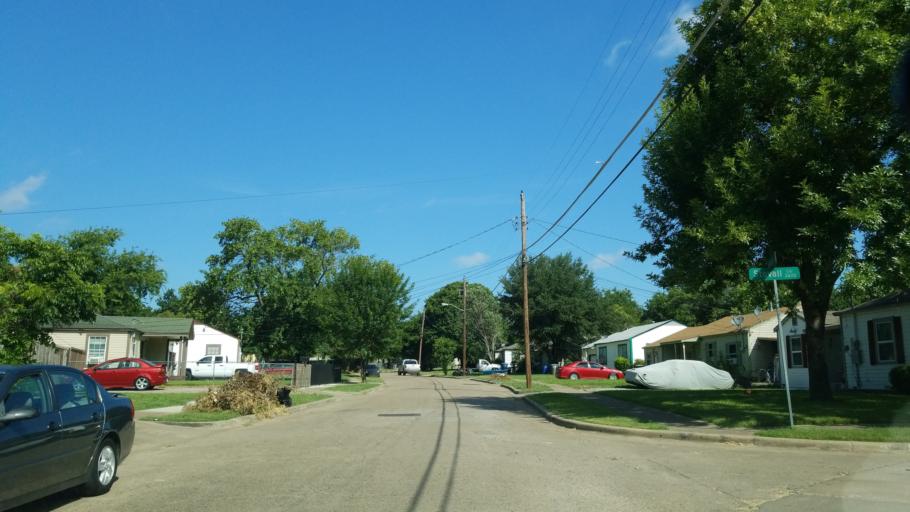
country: US
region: Texas
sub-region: Dallas County
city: Dallas
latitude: 32.7139
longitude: -96.7879
